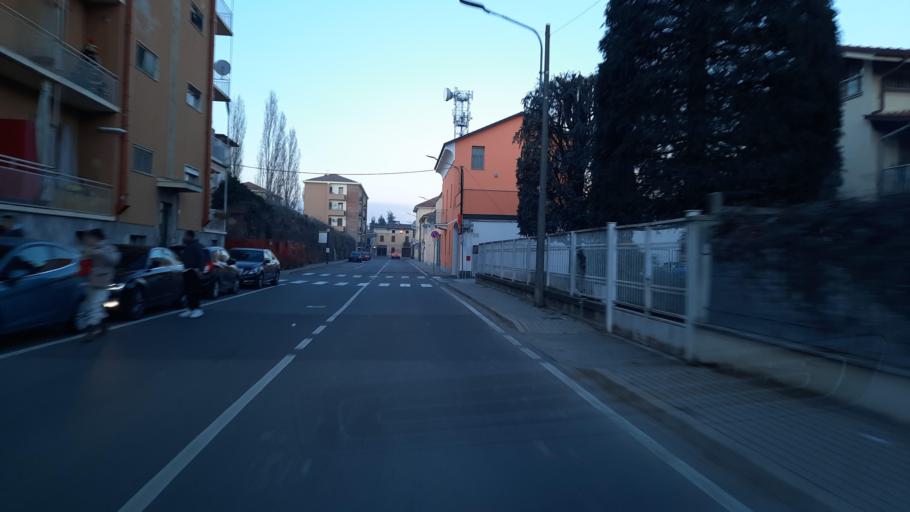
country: IT
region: Piedmont
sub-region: Provincia di Vercelli
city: Trino
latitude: 45.1923
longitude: 8.2994
